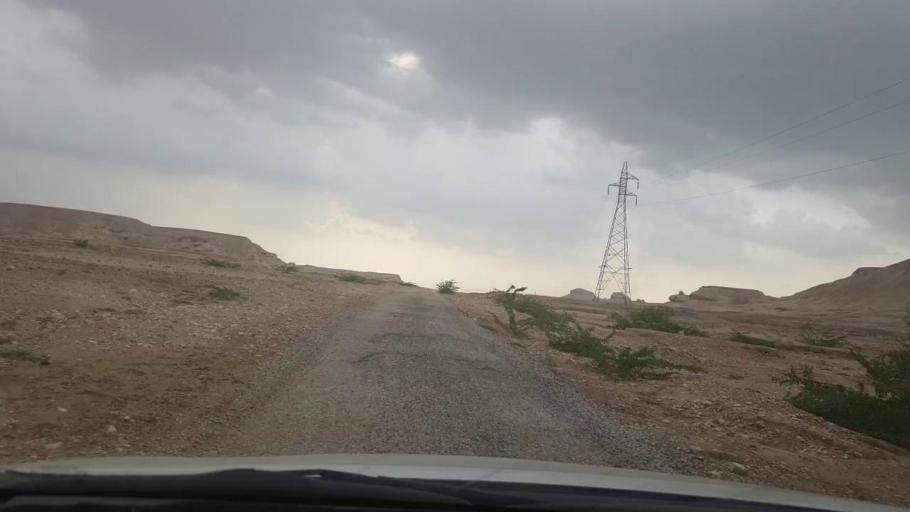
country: PK
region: Sindh
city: Khairpur
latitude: 27.4693
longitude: 68.9053
